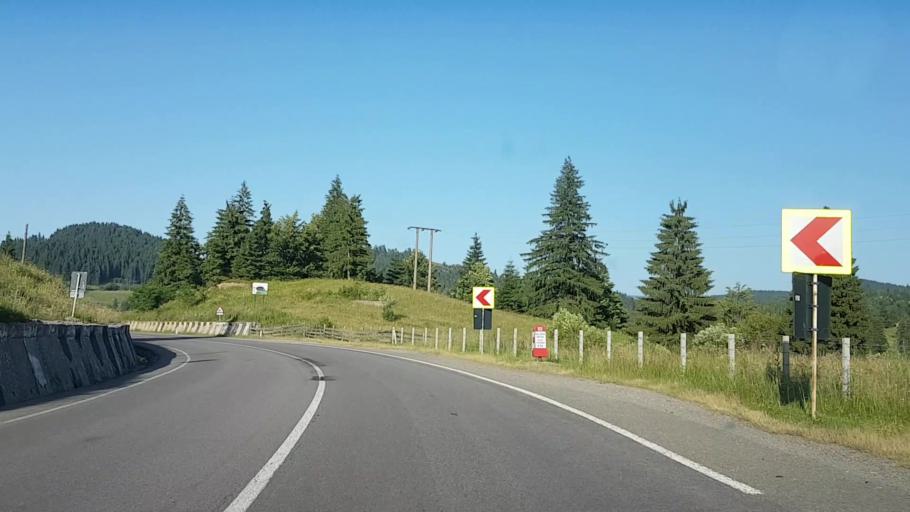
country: RO
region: Bistrita-Nasaud
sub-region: Comuna Tiha Bargaului
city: Tureac
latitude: 47.2217
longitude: 24.9521
